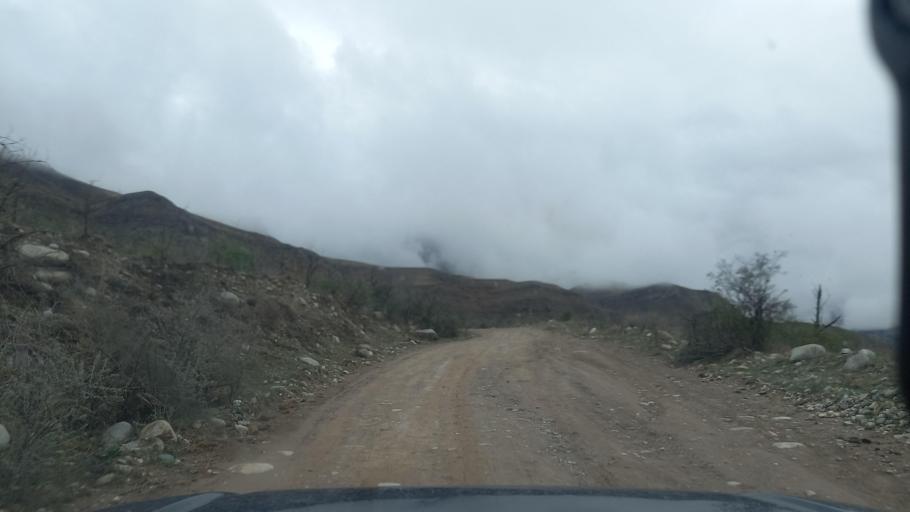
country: RU
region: Kabardino-Balkariya
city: Bylym
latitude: 43.4613
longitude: 43.0110
